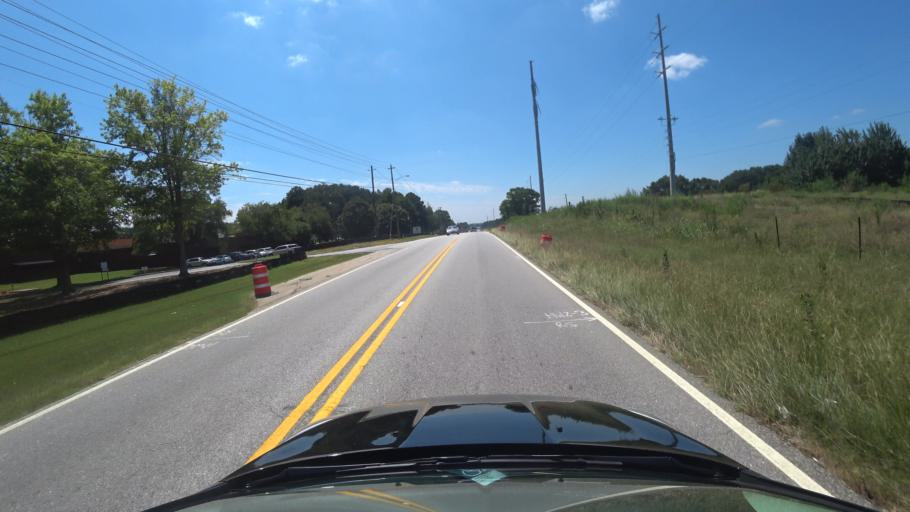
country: US
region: Georgia
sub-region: Newton County
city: Oxford
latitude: 33.6225
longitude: -83.8366
